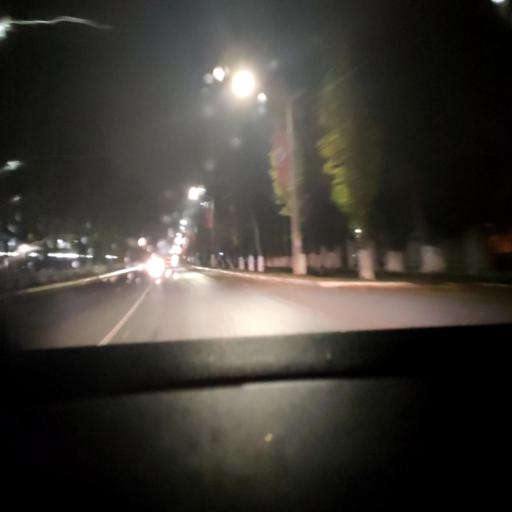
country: RU
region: Voronezj
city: Semiluki
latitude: 51.6826
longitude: 39.0294
